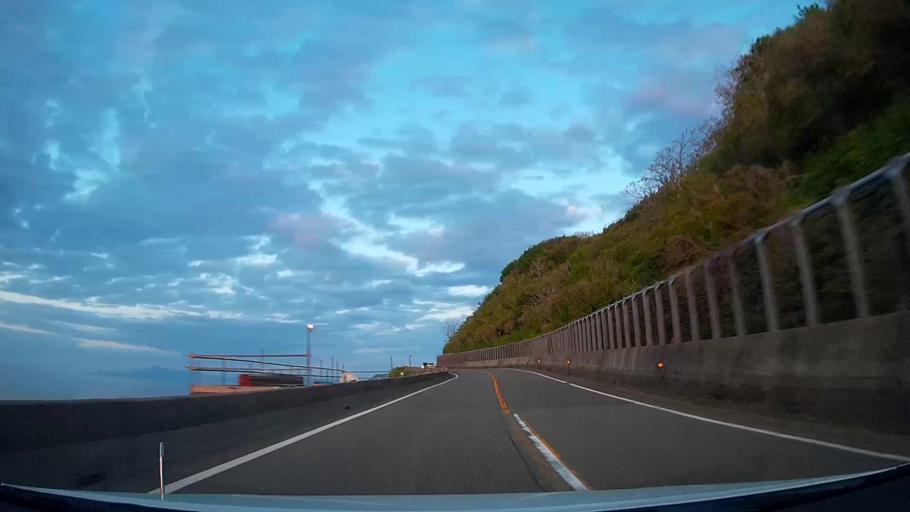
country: JP
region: Niigata
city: Joetsu
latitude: 37.1706
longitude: 138.1178
